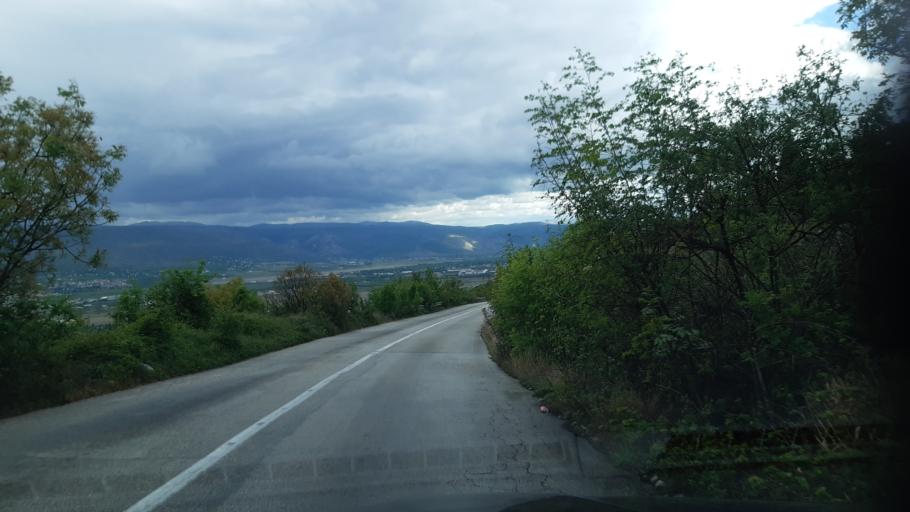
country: BA
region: Federation of Bosnia and Herzegovina
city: Rodoc
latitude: 43.3109
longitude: 17.7779
